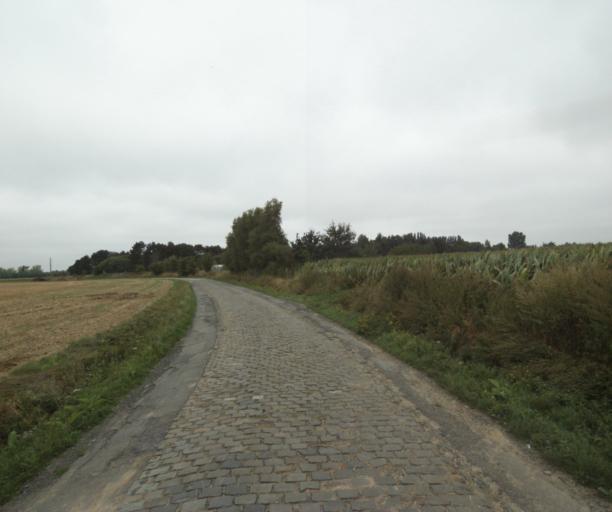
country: FR
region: Nord-Pas-de-Calais
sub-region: Departement du Nord
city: Sailly-lez-Lannoy
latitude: 50.6406
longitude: 3.2063
